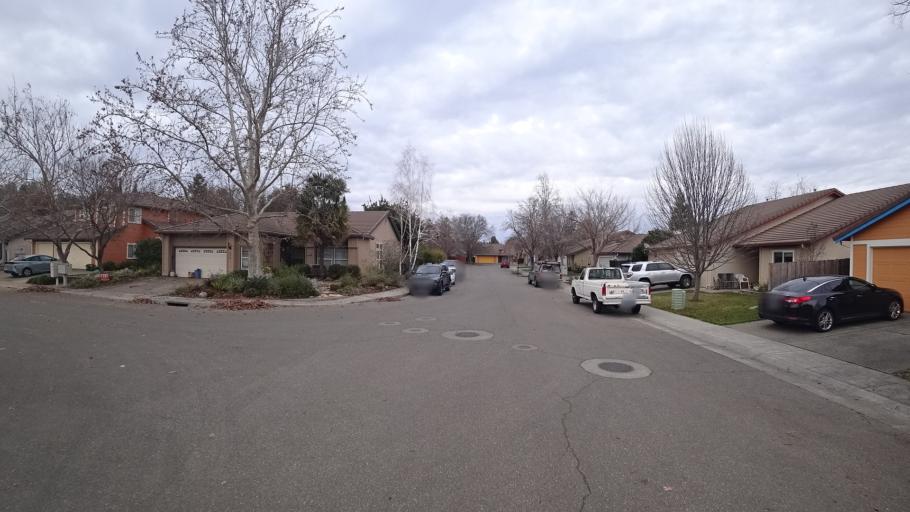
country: US
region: California
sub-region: Yolo County
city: Davis
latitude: 38.5541
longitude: -121.7173
